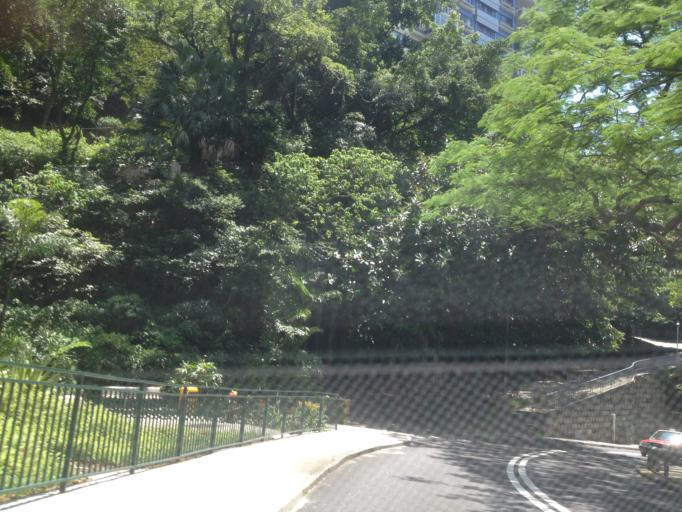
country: HK
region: Central and Western
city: Central
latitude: 22.2732
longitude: 114.1602
